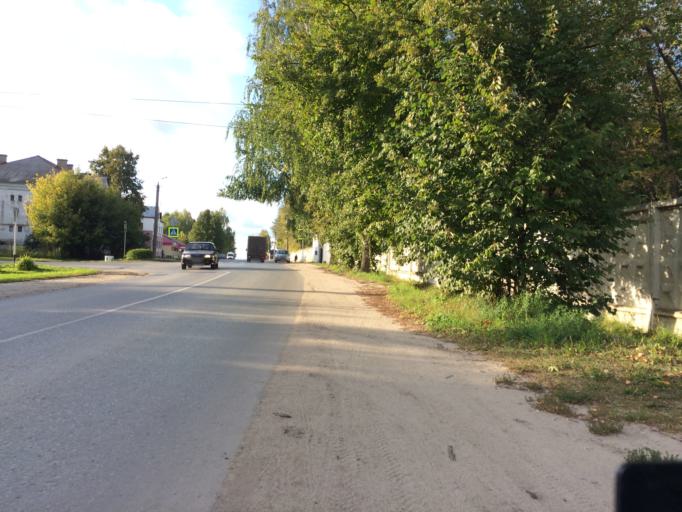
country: RU
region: Mariy-El
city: Yoshkar-Ola
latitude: 56.6529
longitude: 47.9786
